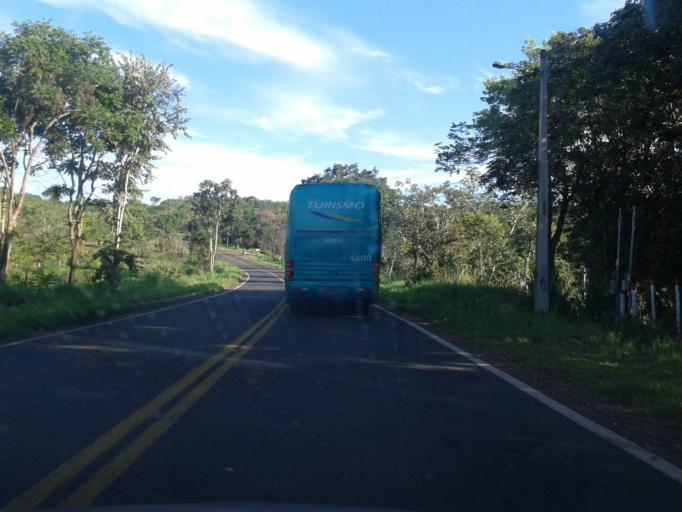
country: BR
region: Minas Gerais
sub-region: Tupaciguara
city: Tupaciguara
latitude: -18.3063
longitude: -48.5610
